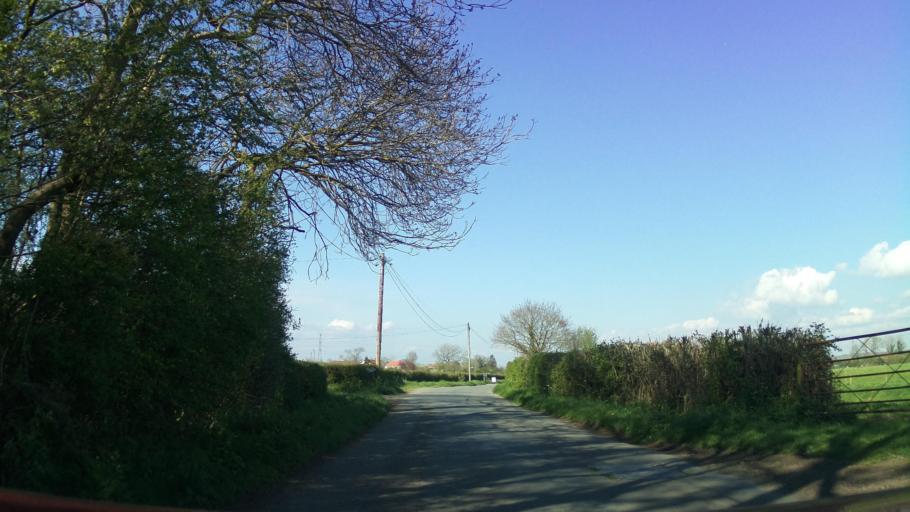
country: GB
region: England
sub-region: South Gloucestershire
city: Hill
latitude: 51.6350
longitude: -2.5533
